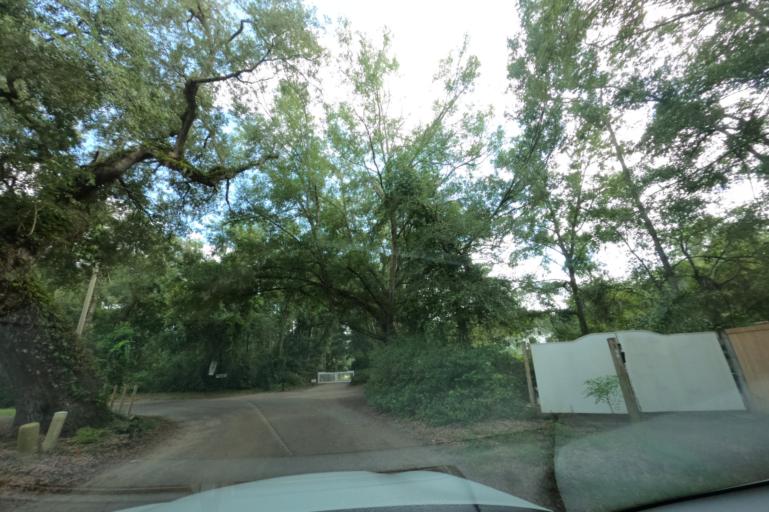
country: US
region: South Carolina
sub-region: Charleston County
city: Shell Point
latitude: 32.7172
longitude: -80.0861
